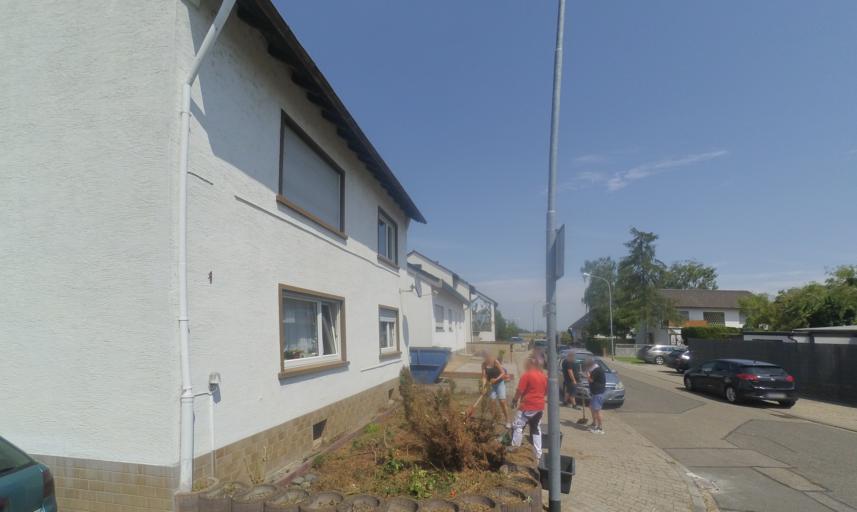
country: DE
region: Rheinland-Pfalz
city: Frankenthal
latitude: 49.5111
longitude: 8.3364
